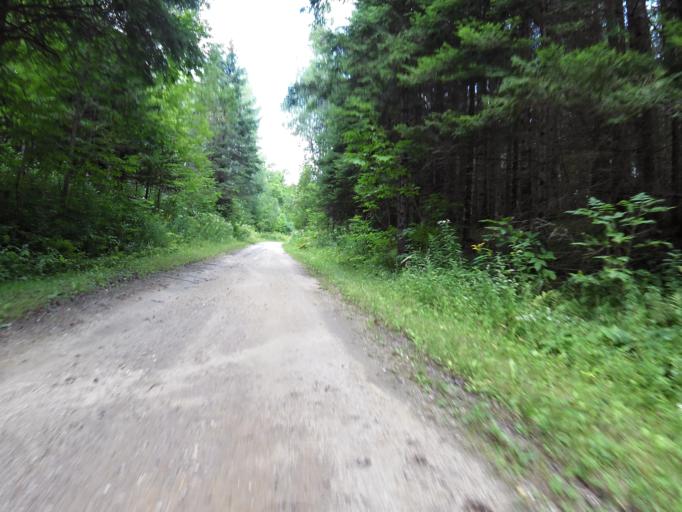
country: CA
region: Quebec
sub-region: Outaouais
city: Maniwaki
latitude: 46.0848
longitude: -76.0673
